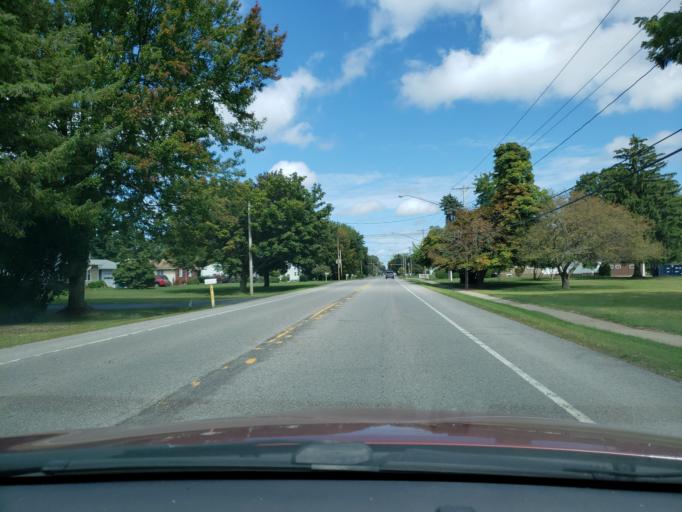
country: US
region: New York
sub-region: Monroe County
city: Greece
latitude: 43.2293
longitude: -77.7336
